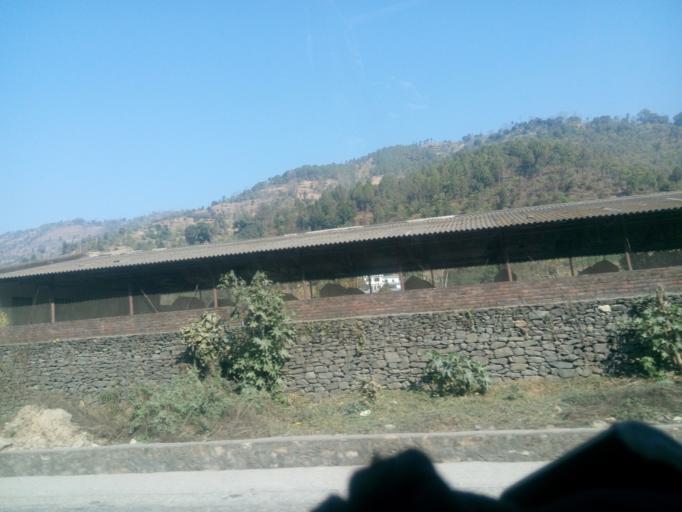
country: NP
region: Central Region
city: Kirtipur
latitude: 27.7374
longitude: 85.1268
